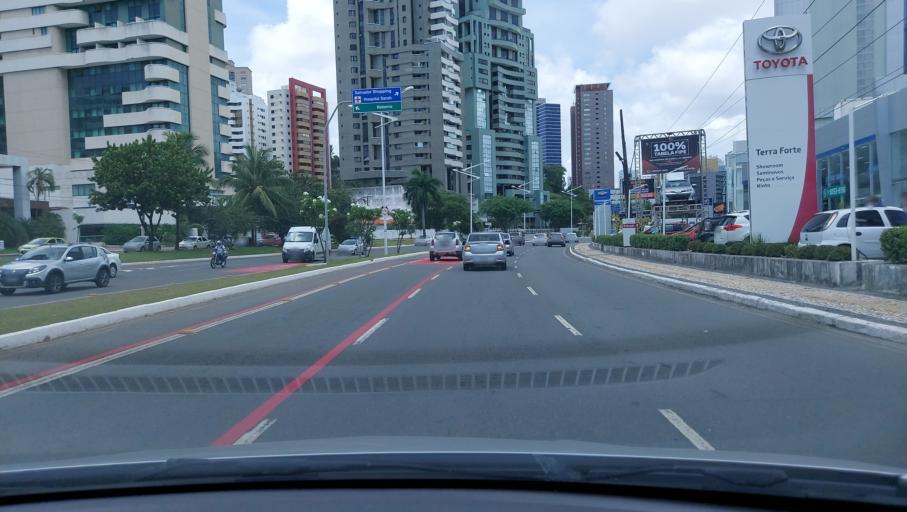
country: BR
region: Bahia
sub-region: Salvador
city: Salvador
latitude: -12.9870
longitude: -38.4507
